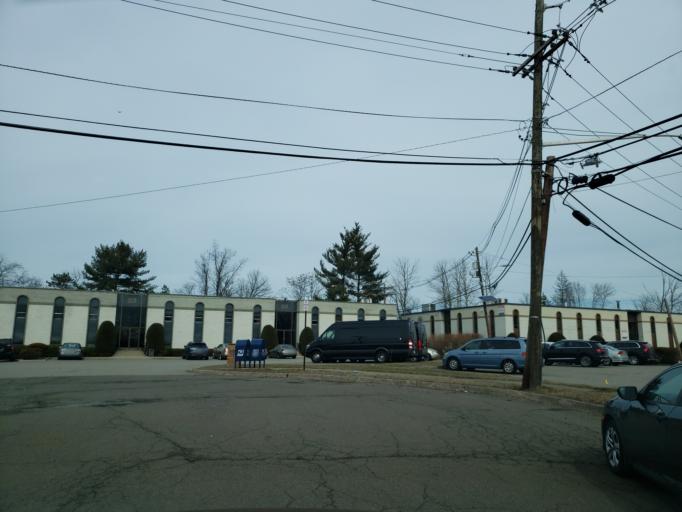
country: US
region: New Jersey
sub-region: Passaic County
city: Singac
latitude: 40.8974
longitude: -74.2446
